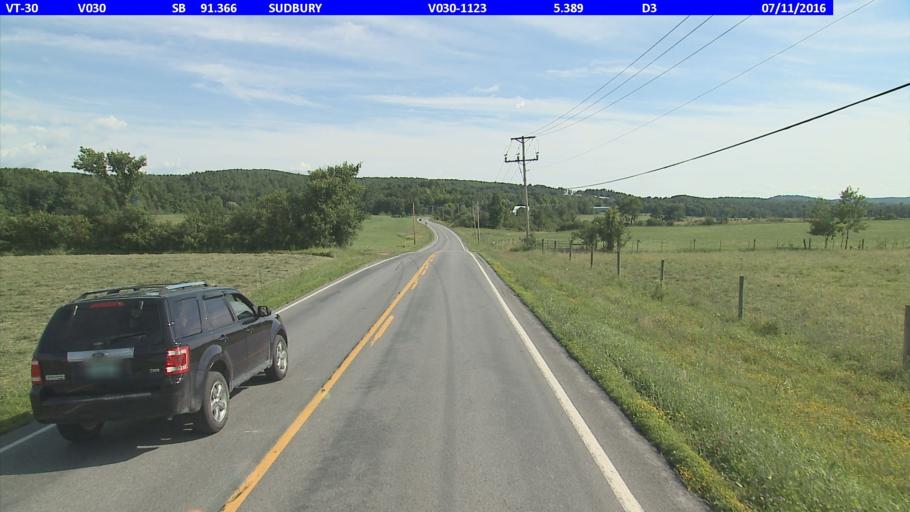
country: US
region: Vermont
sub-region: Rutland County
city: Brandon
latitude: 43.8237
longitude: -73.1935
